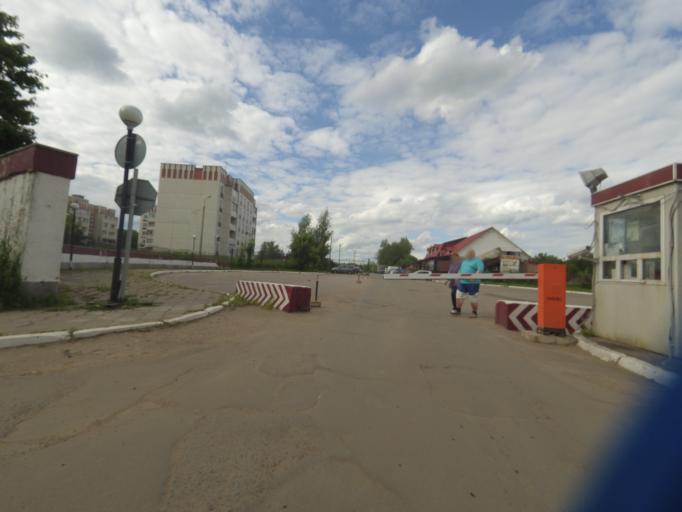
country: RU
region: Moskovskaya
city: Marfino
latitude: 56.0841
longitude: 37.5597
